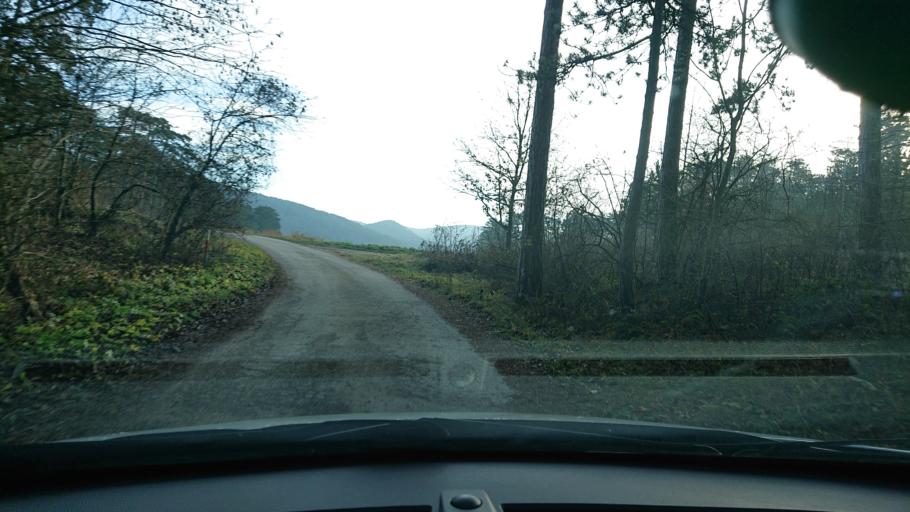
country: AT
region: Lower Austria
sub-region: Politischer Bezirk Baden
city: Berndorf
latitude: 47.9300
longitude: 16.1033
